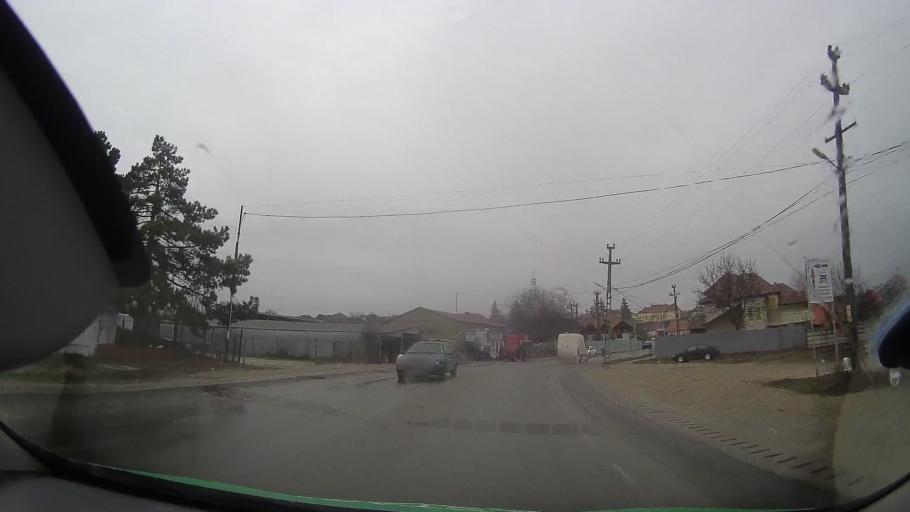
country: RO
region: Bihor
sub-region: Comuna Tinca
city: Tinca
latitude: 46.7712
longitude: 21.9306
